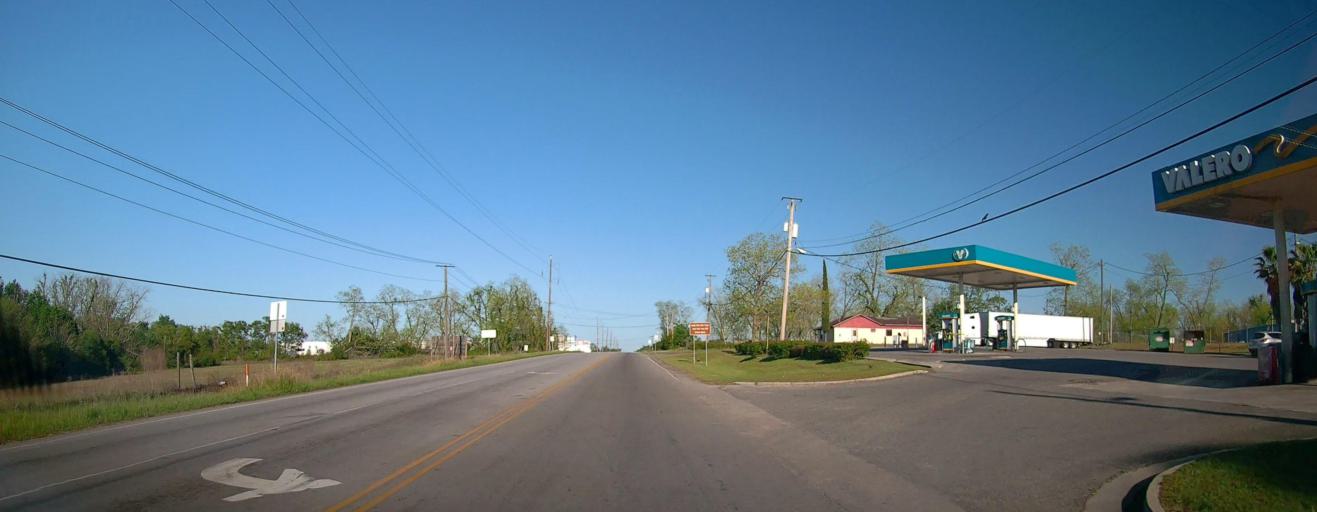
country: US
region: Georgia
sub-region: Ben Hill County
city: Fitzgerald
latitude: 31.7139
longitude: -83.2355
